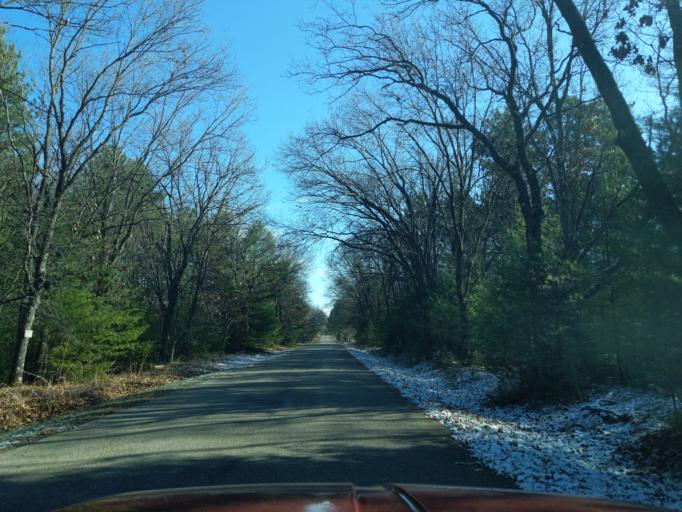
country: US
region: Wisconsin
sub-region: Waushara County
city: Silver Lake
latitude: 44.1052
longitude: -89.1706
